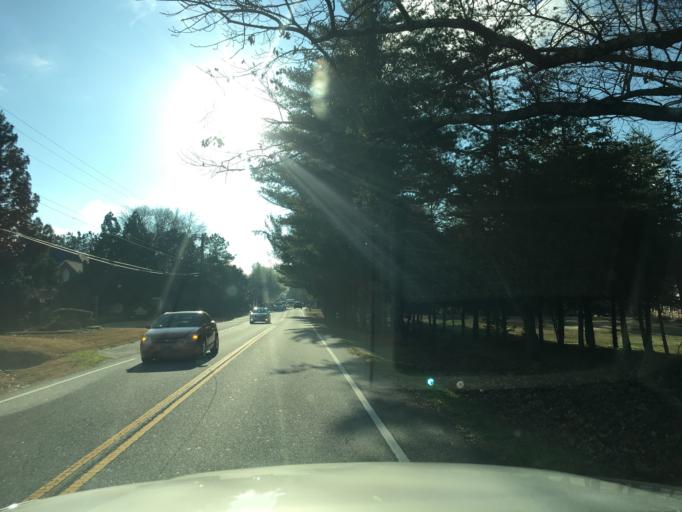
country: US
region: South Carolina
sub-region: Greenville County
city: Wade Hampton
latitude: 34.8753
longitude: -82.3041
